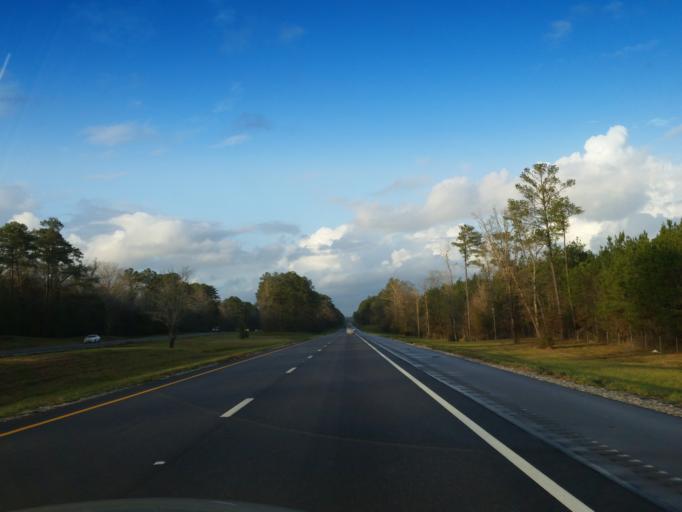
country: US
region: Mississippi
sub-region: Jones County
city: Sharon
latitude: 31.8406
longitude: -89.0493
